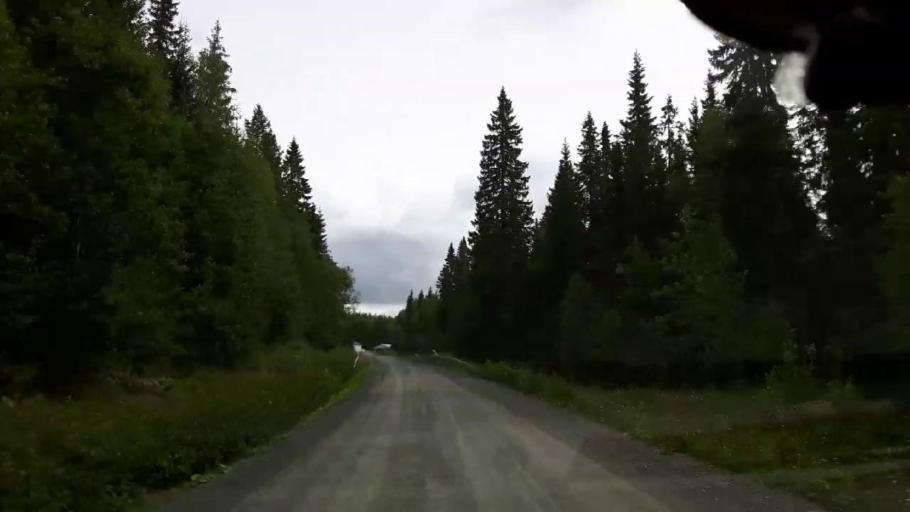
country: SE
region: Jaemtland
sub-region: Krokoms Kommun
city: Valla
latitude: 63.6378
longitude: 14.0104
